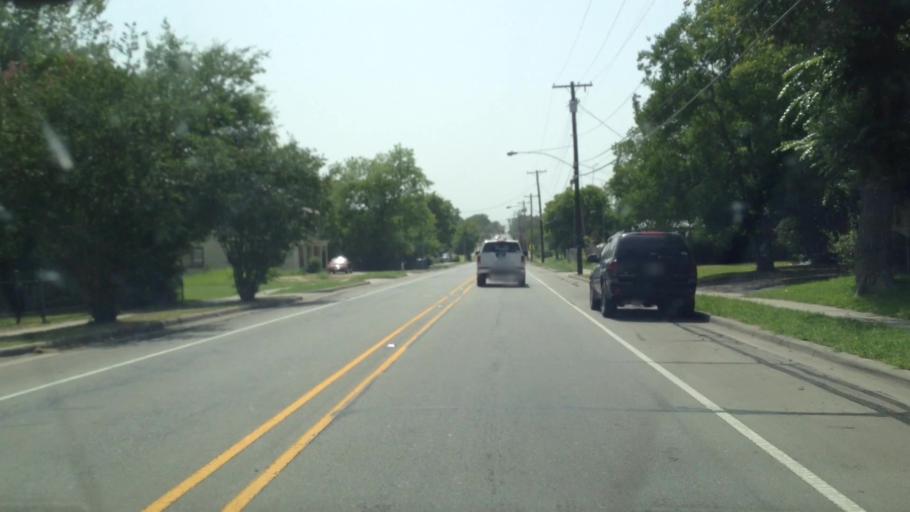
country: US
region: Texas
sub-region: Hunt County
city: Greenville
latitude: 33.1400
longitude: -96.1164
